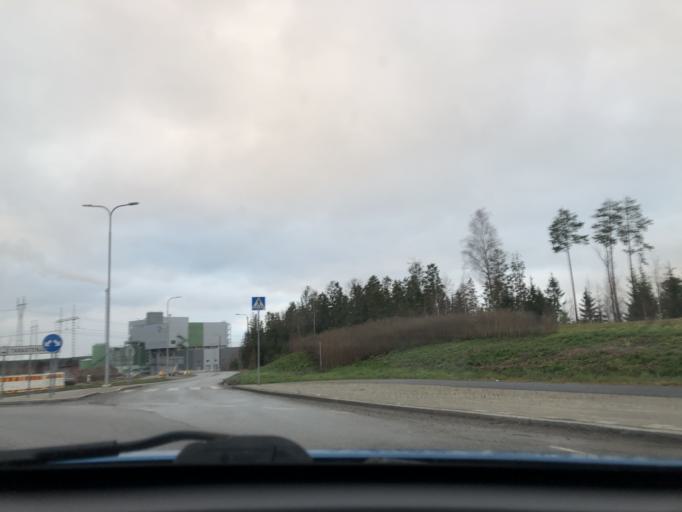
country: FI
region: Pirkanmaa
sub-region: Tampere
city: Kangasala
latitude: 61.5396
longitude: 23.9790
